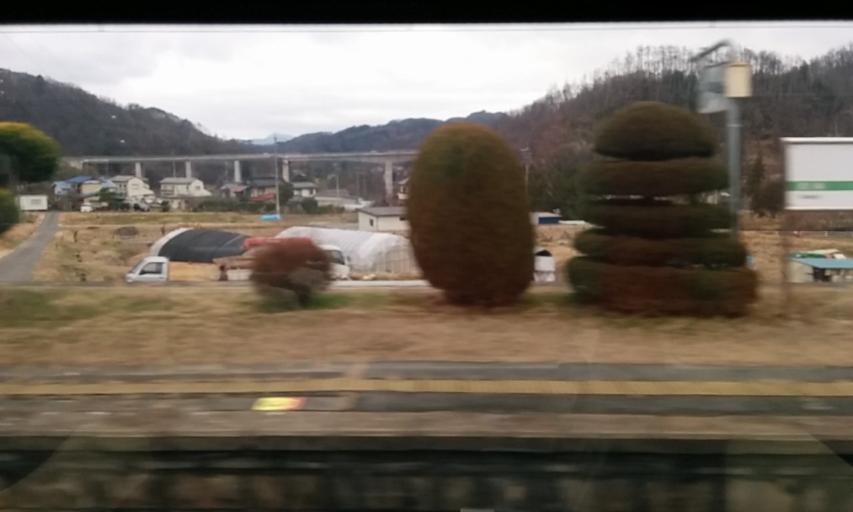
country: JP
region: Nagano
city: Hotaka
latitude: 36.4310
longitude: 138.0161
